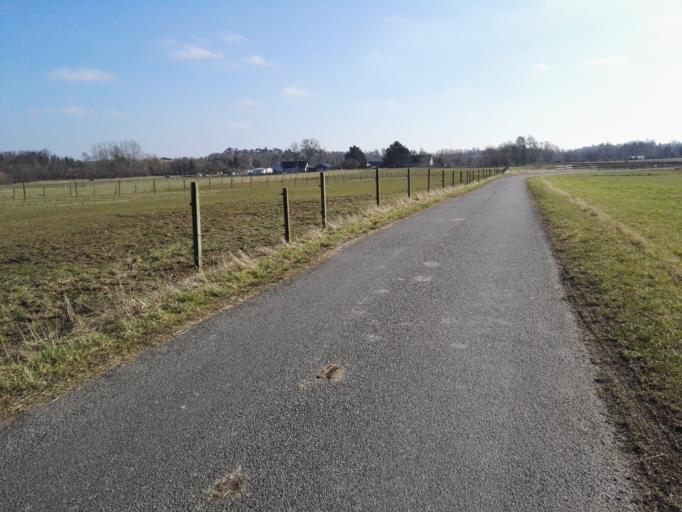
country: DK
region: Capital Region
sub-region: Frederikssund Kommune
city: Frederikssund
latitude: 55.7889
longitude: 12.0299
